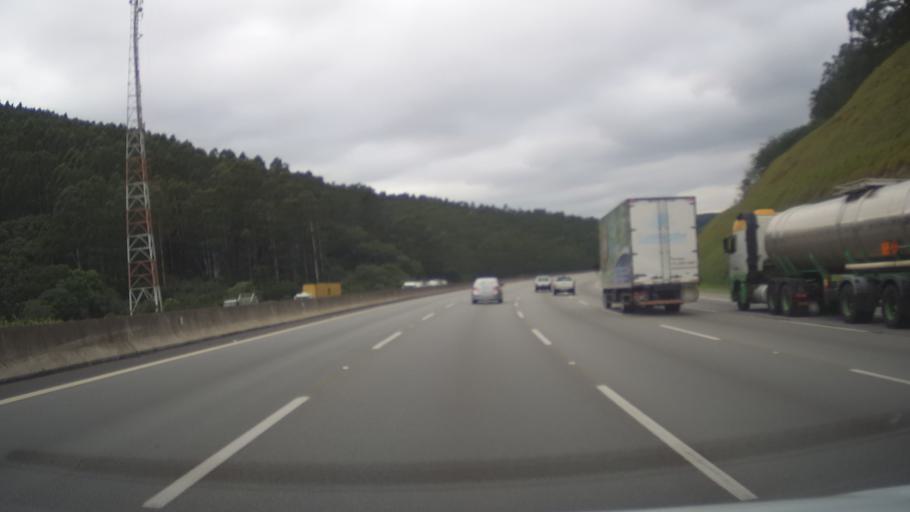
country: BR
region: Sao Paulo
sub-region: Caieiras
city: Caieiras
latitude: -23.3581
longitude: -46.7874
